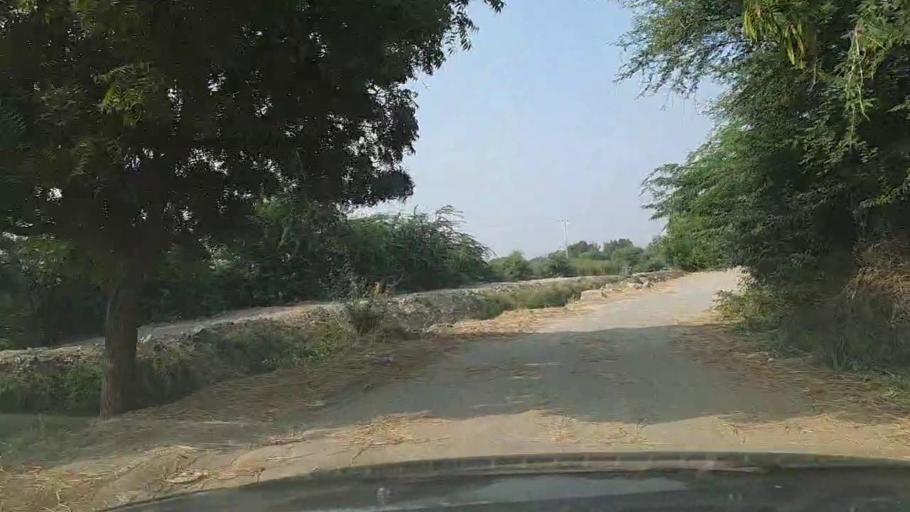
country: PK
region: Sindh
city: Mirpur Batoro
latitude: 24.7048
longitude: 68.2546
